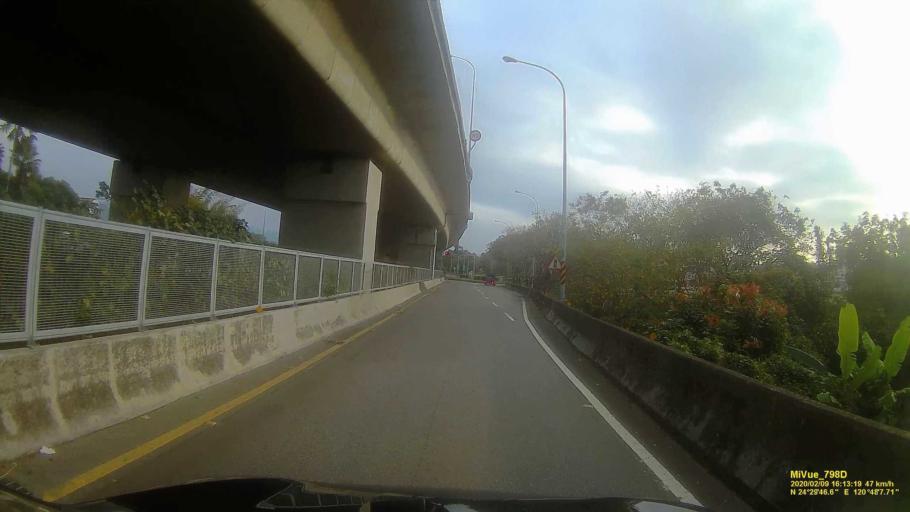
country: TW
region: Taiwan
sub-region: Miaoli
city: Miaoli
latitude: 24.4961
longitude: 120.8021
